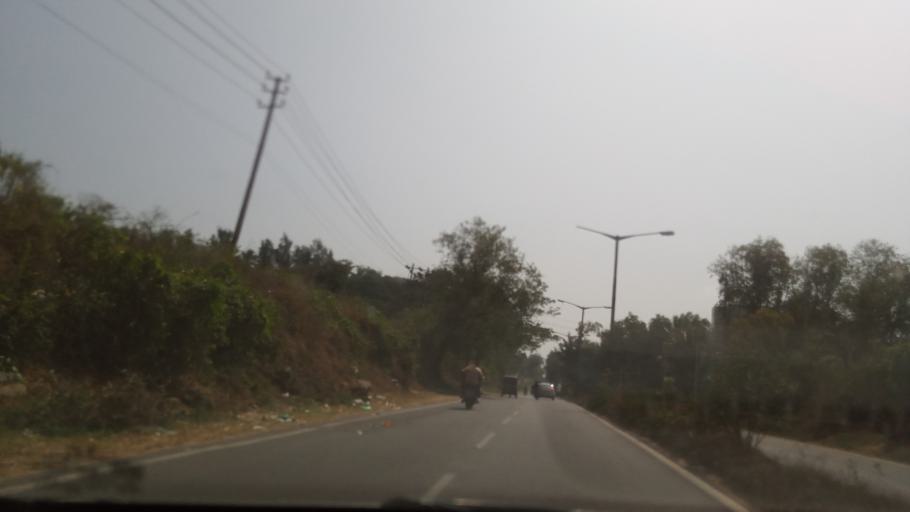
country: IN
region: Karnataka
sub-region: Mysore
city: Mysore
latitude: 12.3336
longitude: 76.6326
